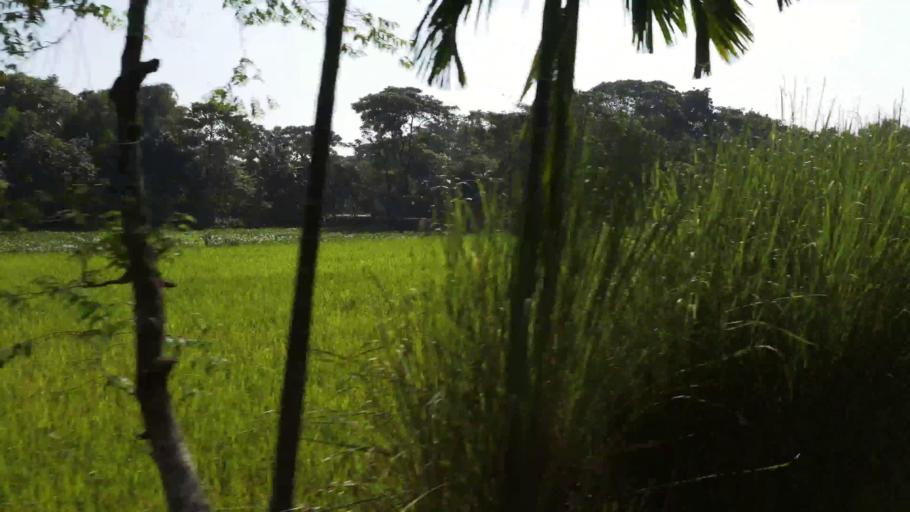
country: BD
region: Dhaka
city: Gafargaon
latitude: 24.5630
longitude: 90.5084
